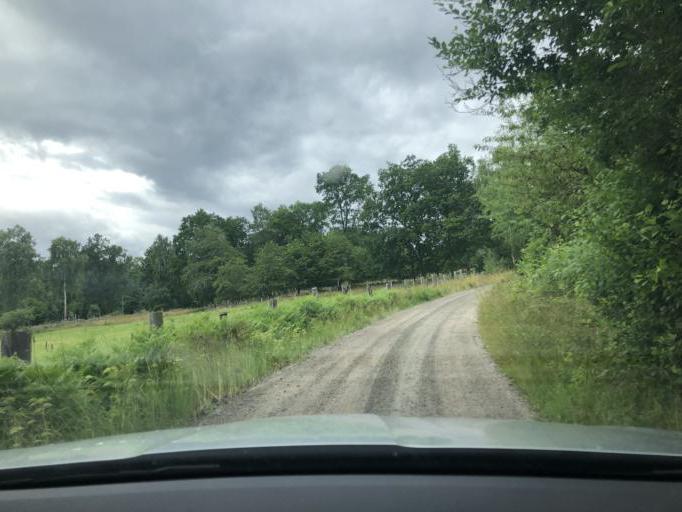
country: SE
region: Blekinge
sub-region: Solvesborgs Kommun
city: Soelvesborg
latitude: 56.1563
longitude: 14.5900
